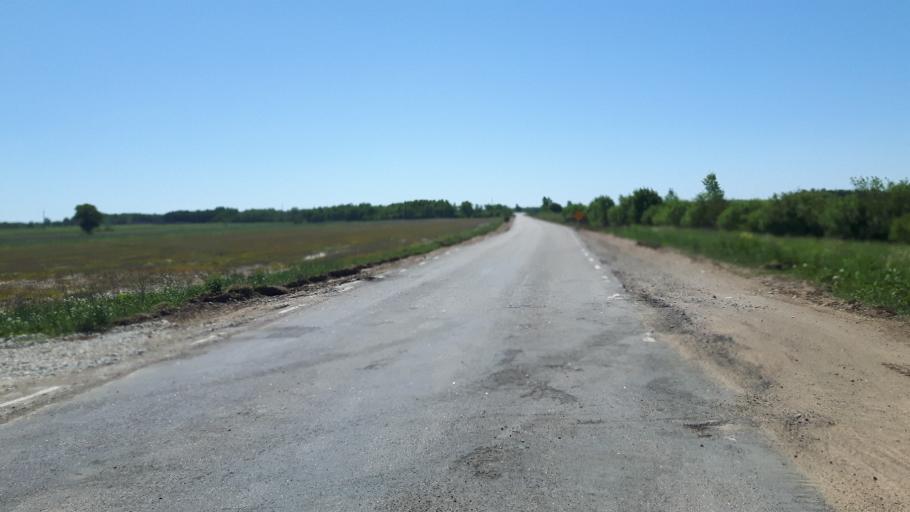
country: EE
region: Ida-Virumaa
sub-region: Narva-Joesuu linn
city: Narva-Joesuu
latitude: 59.3862
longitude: 27.9205
